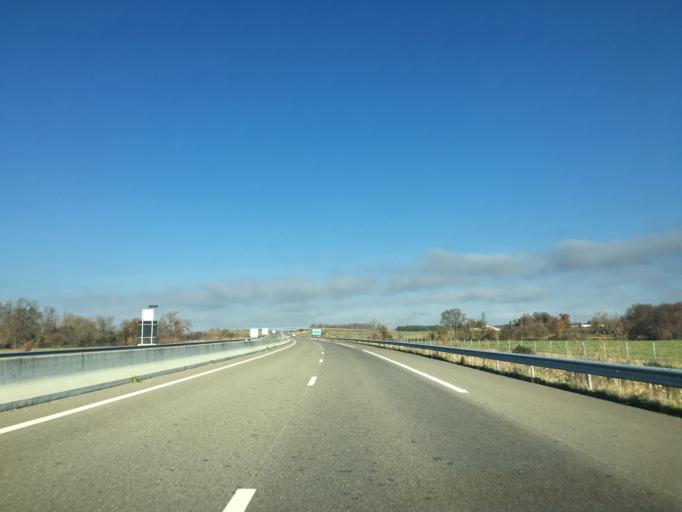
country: FR
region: Midi-Pyrenees
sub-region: Departement du Gers
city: Barcelonne-du-Gers
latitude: 43.7270
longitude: -0.2715
